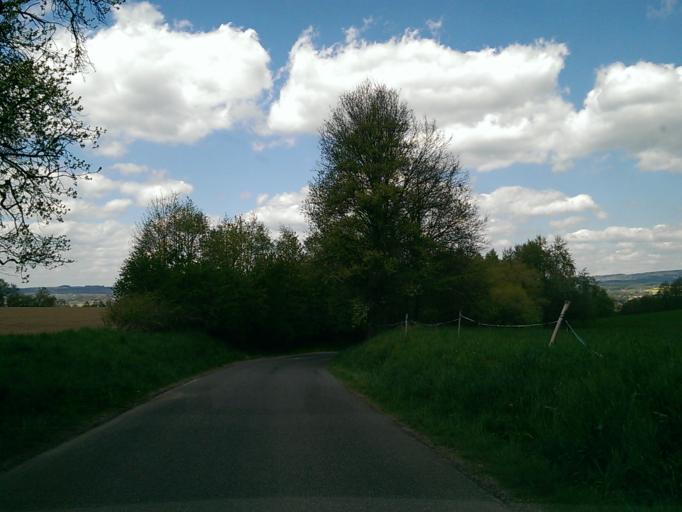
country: CZ
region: Liberecky
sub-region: Okres Semily
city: Turnov
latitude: 50.5611
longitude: 15.1398
